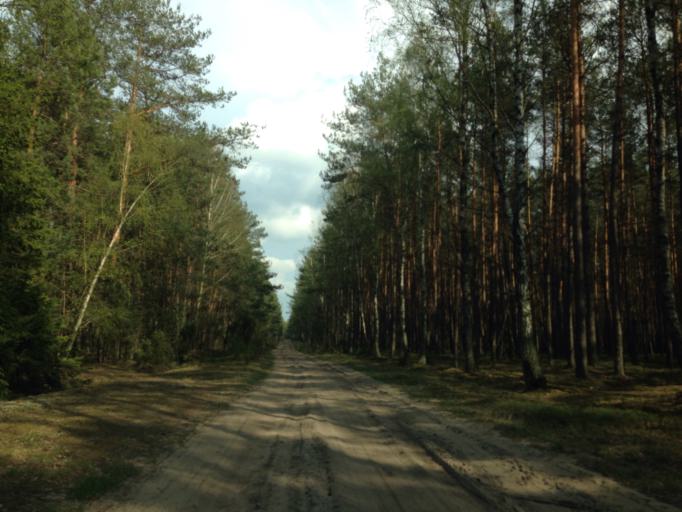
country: PL
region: Kujawsko-Pomorskie
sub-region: Powiat brodnicki
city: Gorzno
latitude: 53.1265
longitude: 19.6840
